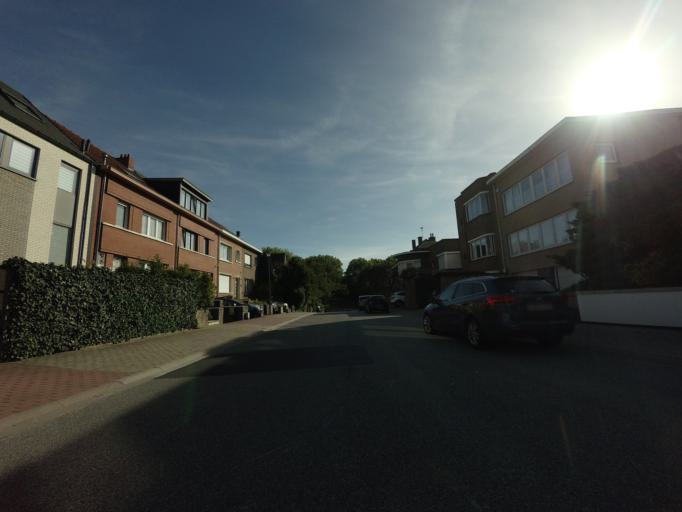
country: BE
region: Flanders
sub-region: Provincie Vlaams-Brabant
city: Kraainem
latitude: 50.8653
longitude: 4.4412
